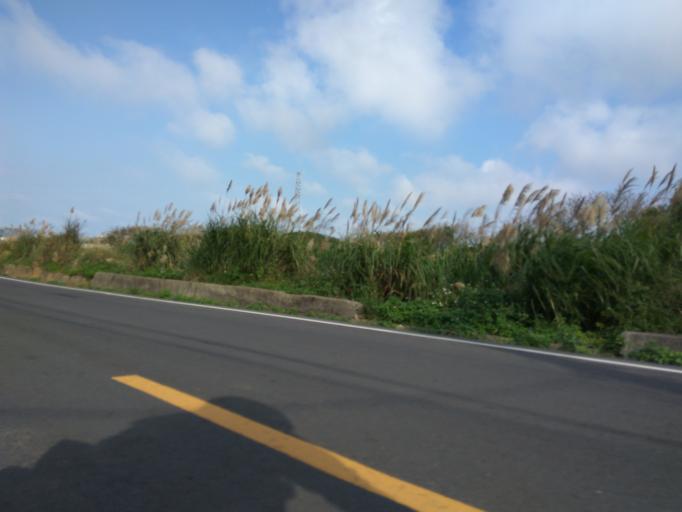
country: TW
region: Taiwan
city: Taoyuan City
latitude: 25.0657
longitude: 121.1724
